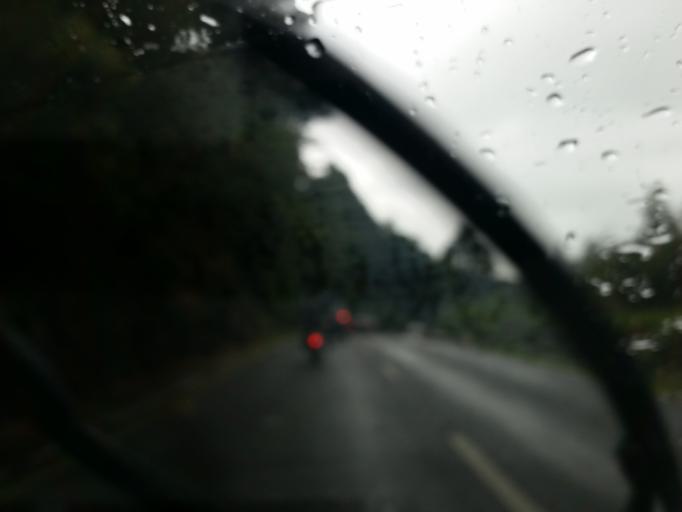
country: NZ
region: Waikato
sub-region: Hauraki District
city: Paeroa
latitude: -37.4206
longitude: 175.7335
